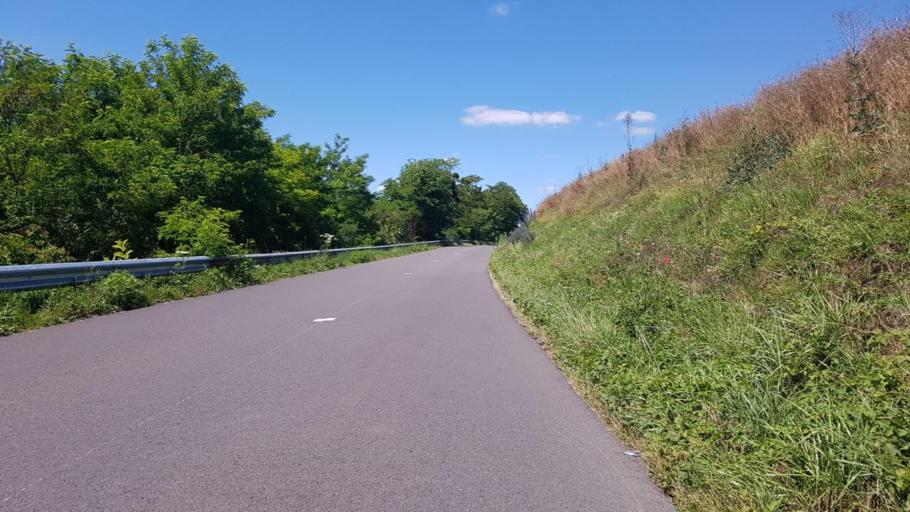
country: FR
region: Ile-de-France
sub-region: Departement de Seine-et-Marne
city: Sammeron
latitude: 48.9541
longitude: 3.0921
